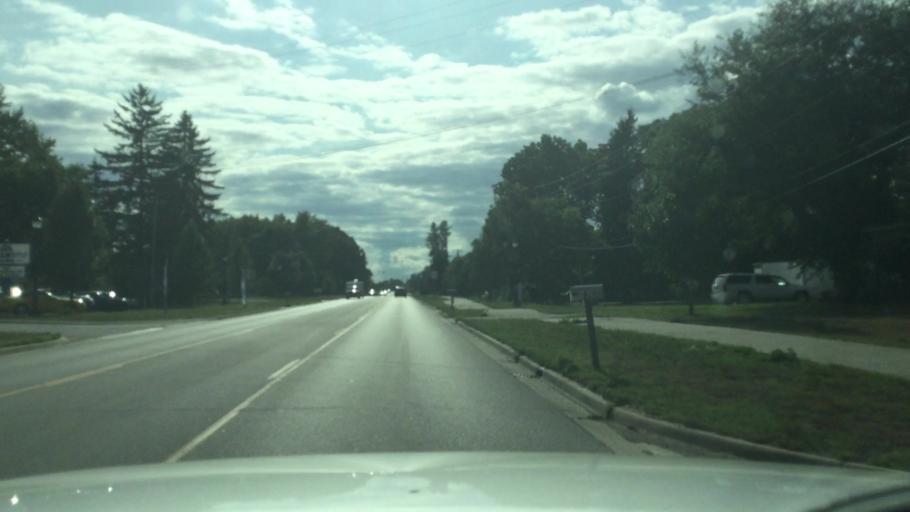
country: US
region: Michigan
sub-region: Ionia County
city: Belding
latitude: 43.0889
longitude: -85.2441
